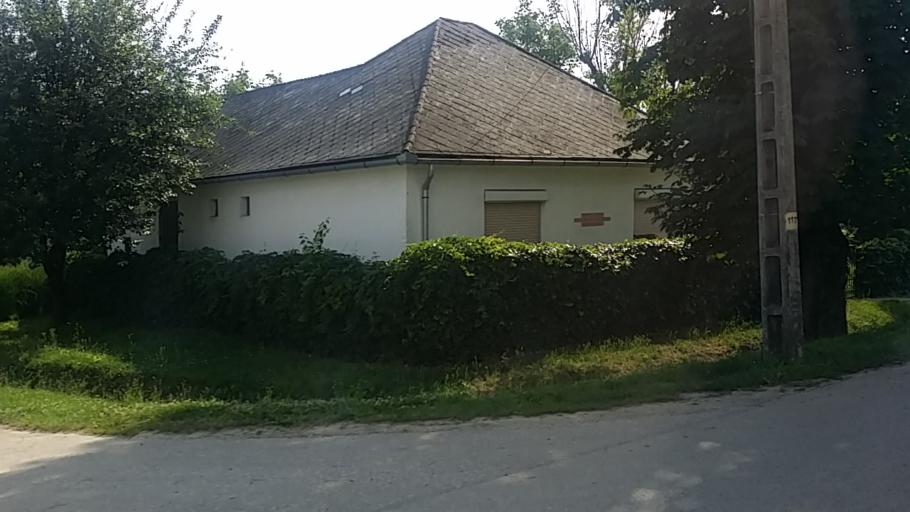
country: HU
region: Tolna
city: Szedres
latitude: 46.4759
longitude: 18.6901
